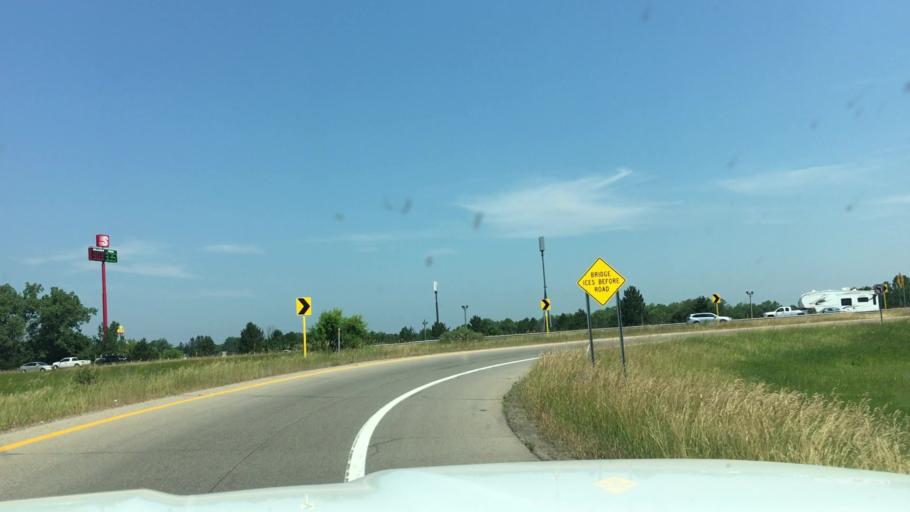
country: US
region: Michigan
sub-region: Ionia County
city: Portland
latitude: 42.8588
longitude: -84.8857
